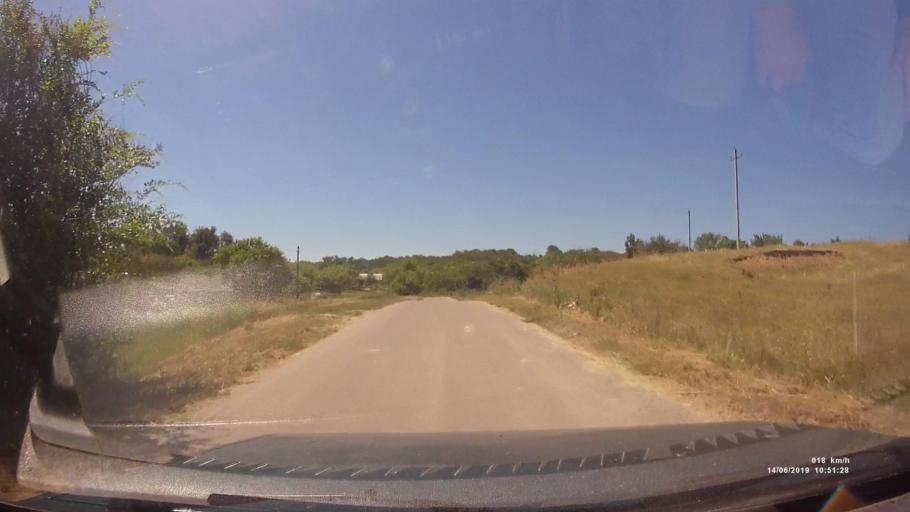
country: RU
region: Rostov
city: Kazanskaya
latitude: 49.8696
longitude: 41.3926
